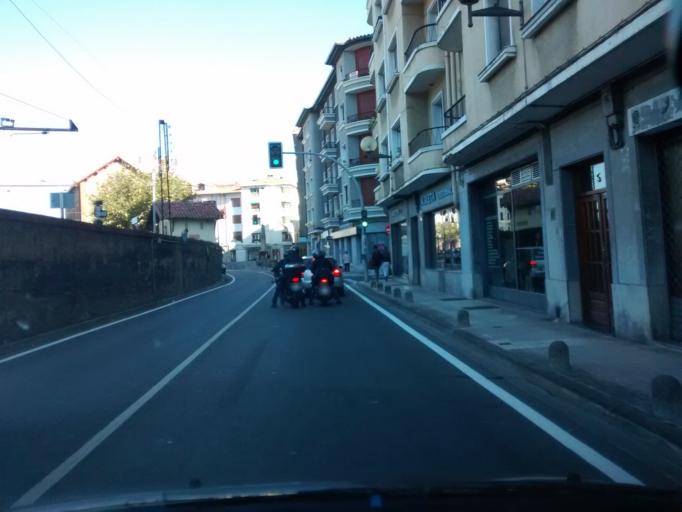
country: ES
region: Basque Country
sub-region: Provincia de Guipuzcoa
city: Deba
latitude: 43.2929
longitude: -2.3557
